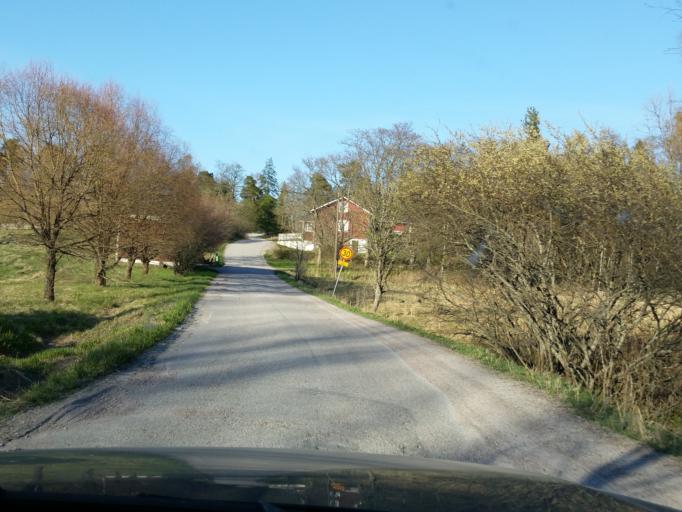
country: FI
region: Uusimaa
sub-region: Helsinki
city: Espoo
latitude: 60.0987
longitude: 24.5747
